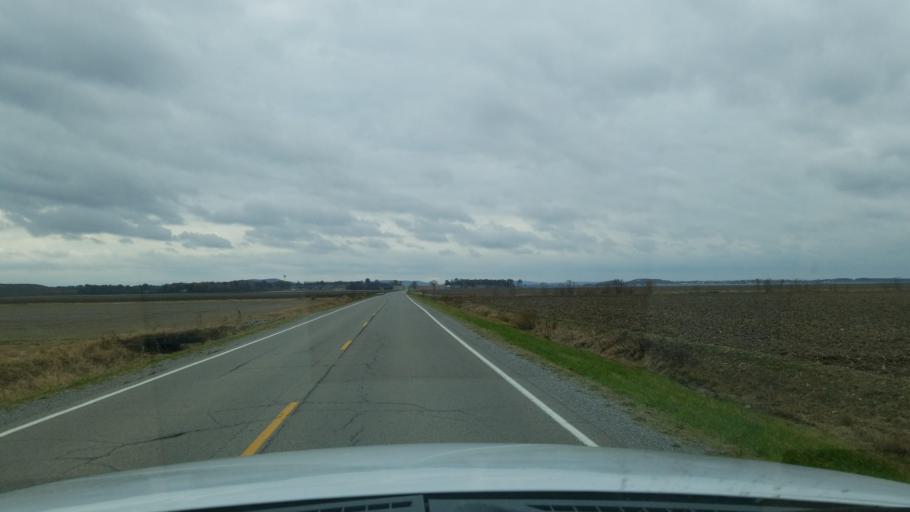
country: US
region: Illinois
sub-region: Saline County
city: Eldorado
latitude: 37.7740
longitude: -88.4382
